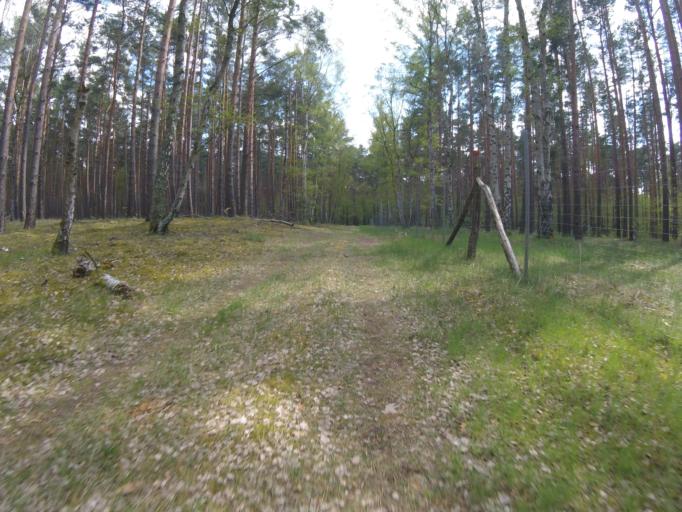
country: DE
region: Brandenburg
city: Gross Koris
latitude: 52.2120
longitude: 13.7317
